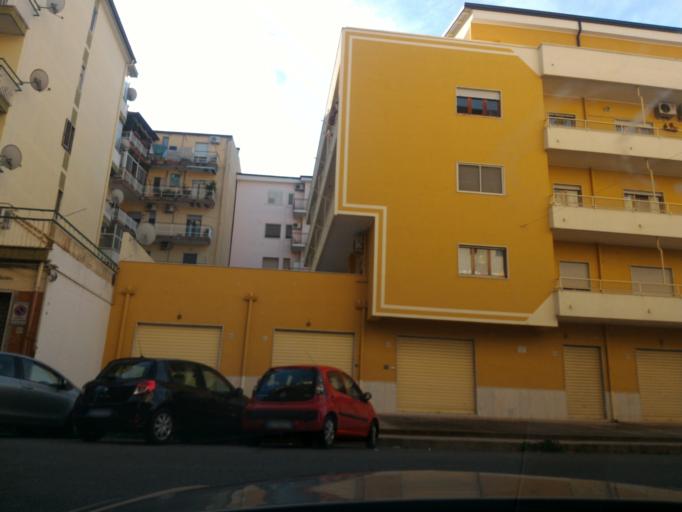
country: IT
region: Calabria
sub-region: Provincia di Crotone
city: Crotone
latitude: 39.0809
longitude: 17.1115
